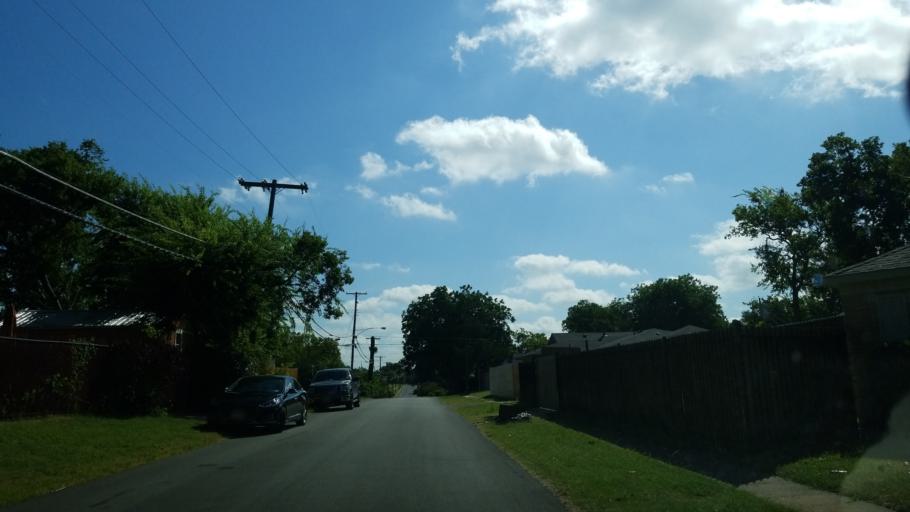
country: US
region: Texas
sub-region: Dallas County
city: Dallas
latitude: 32.7158
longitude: -96.7958
